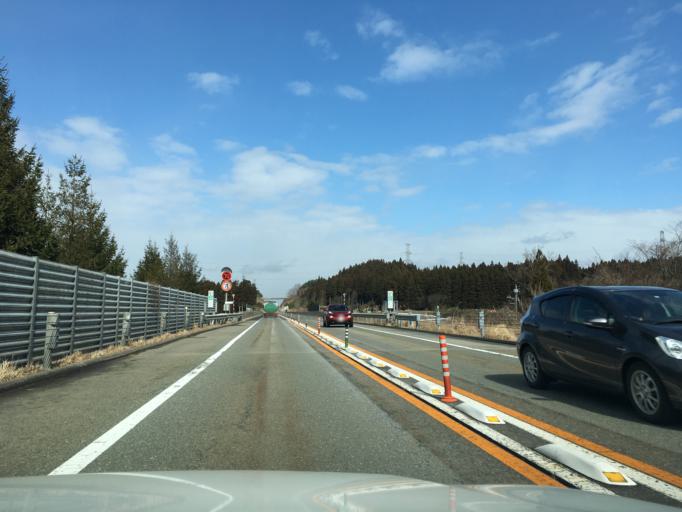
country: JP
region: Akita
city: Akita Shi
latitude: 39.8025
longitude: 140.0973
